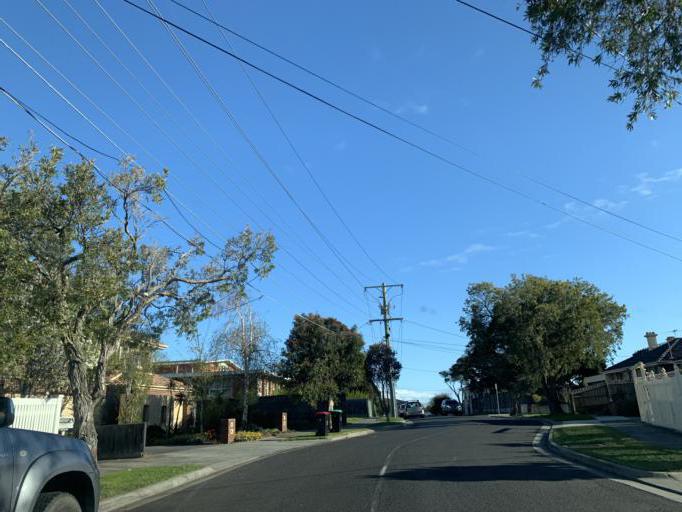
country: AU
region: Victoria
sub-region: Kingston
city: Mentone
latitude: -37.9871
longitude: 145.0659
